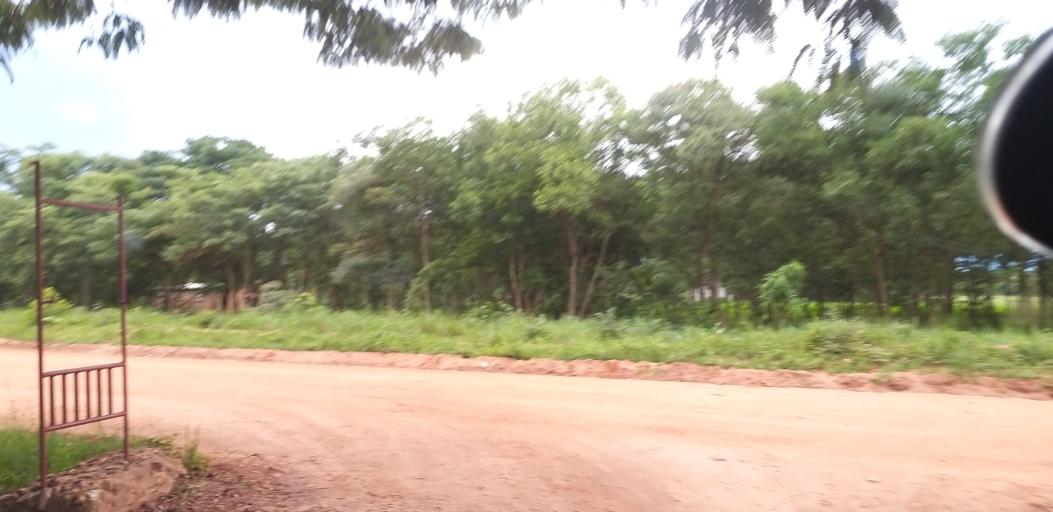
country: ZM
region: Lusaka
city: Chongwe
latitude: -15.1762
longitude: 28.4612
